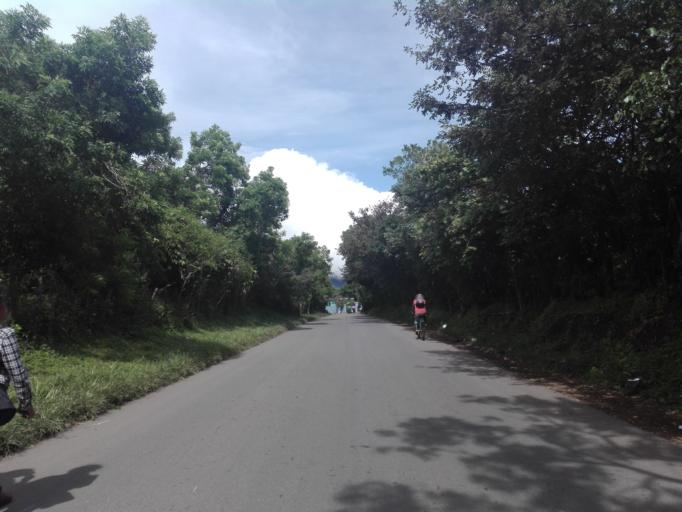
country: GT
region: Escuintla
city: San Vicente Pacaya
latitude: 14.3694
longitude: -90.5614
